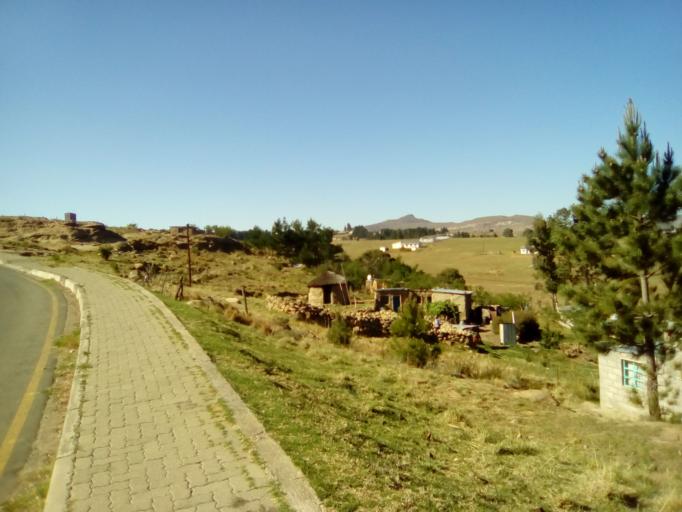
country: LS
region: Qacha's Nek
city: Qacha's Nek
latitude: -30.1040
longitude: 28.6782
